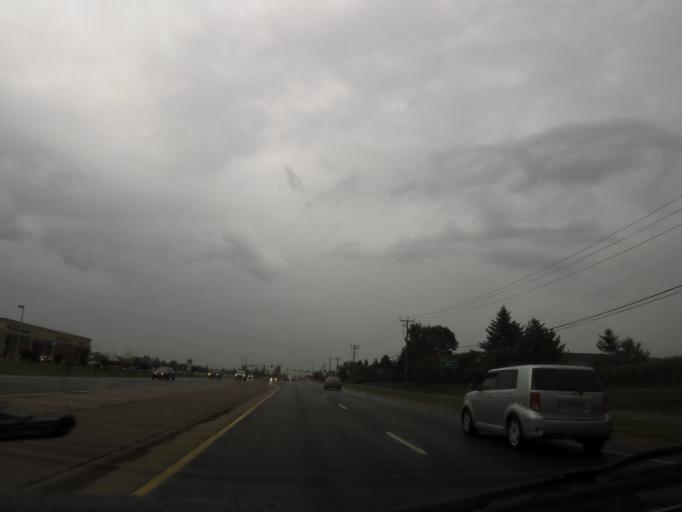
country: US
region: Minnesota
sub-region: Washington County
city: Woodbury
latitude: 44.9393
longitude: -92.9035
